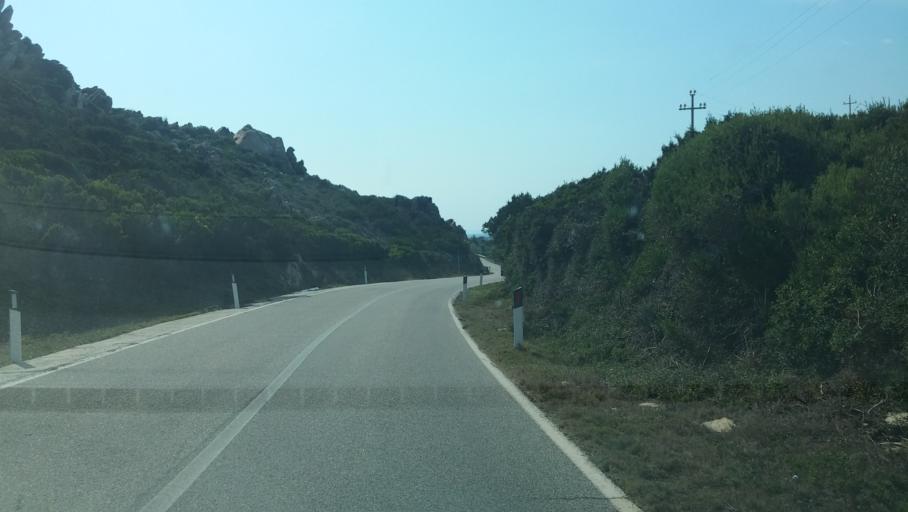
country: IT
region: Sardinia
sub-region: Provincia di Olbia-Tempio
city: La Maddalena
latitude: 41.2574
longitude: 9.4211
